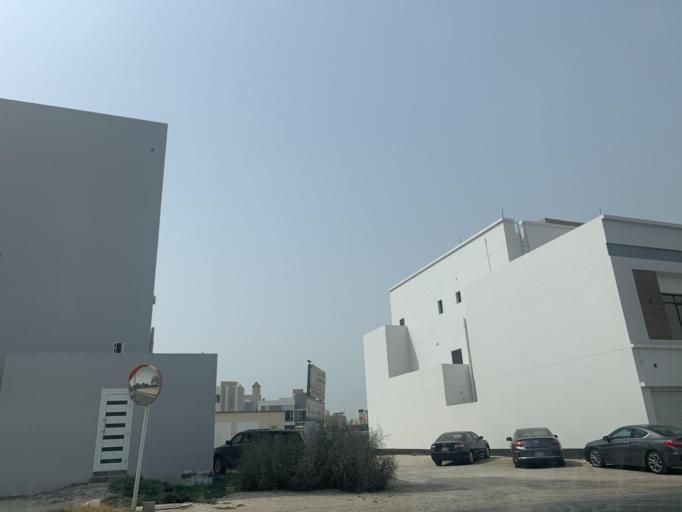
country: BH
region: Manama
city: Jidd Hafs
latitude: 26.1982
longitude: 50.4686
